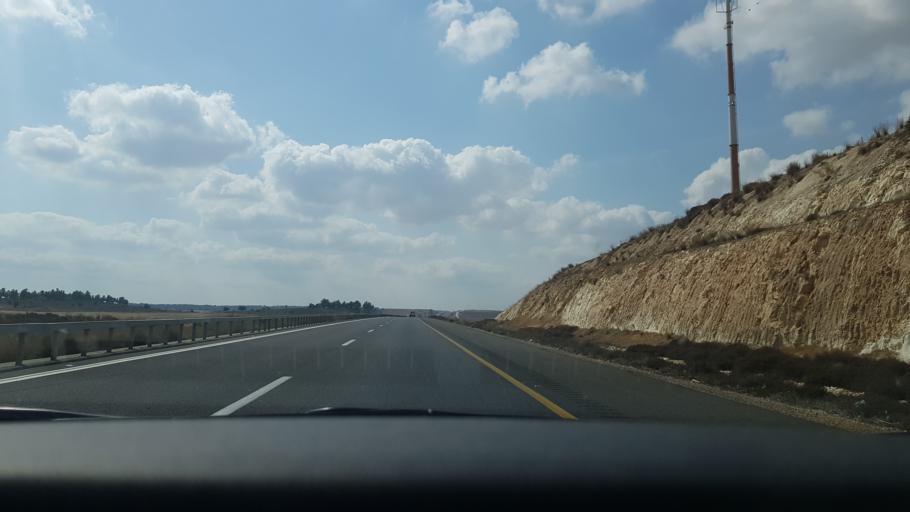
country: IL
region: Southern District
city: Qiryat Gat
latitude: 31.5714
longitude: 34.8056
